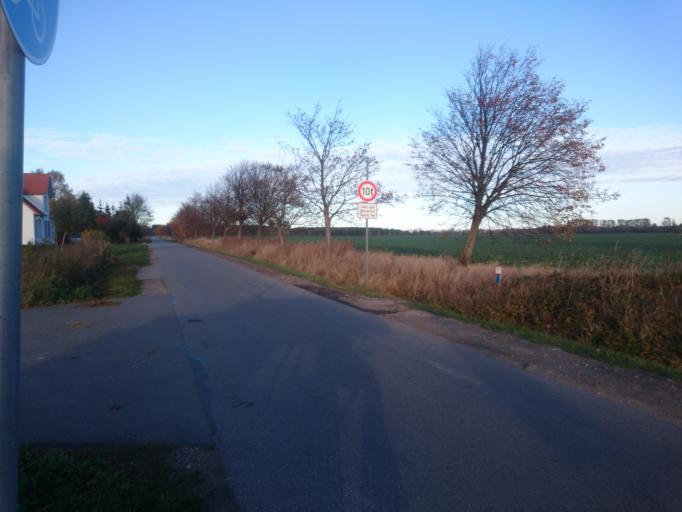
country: DE
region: Mecklenburg-Vorpommern
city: Borgerende-Rethwisch
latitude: 54.1416
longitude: 11.9596
